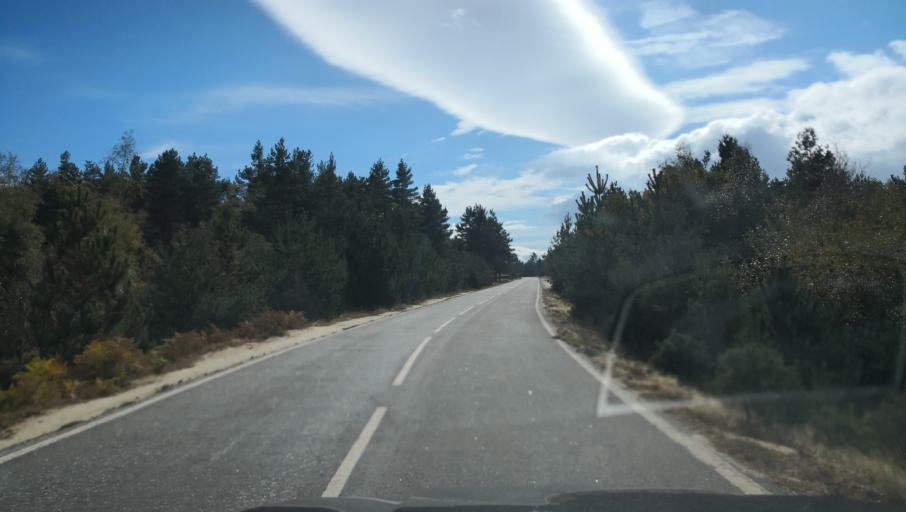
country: PT
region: Vila Real
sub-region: Vila Real
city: Vila Real
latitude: 41.3548
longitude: -7.7919
